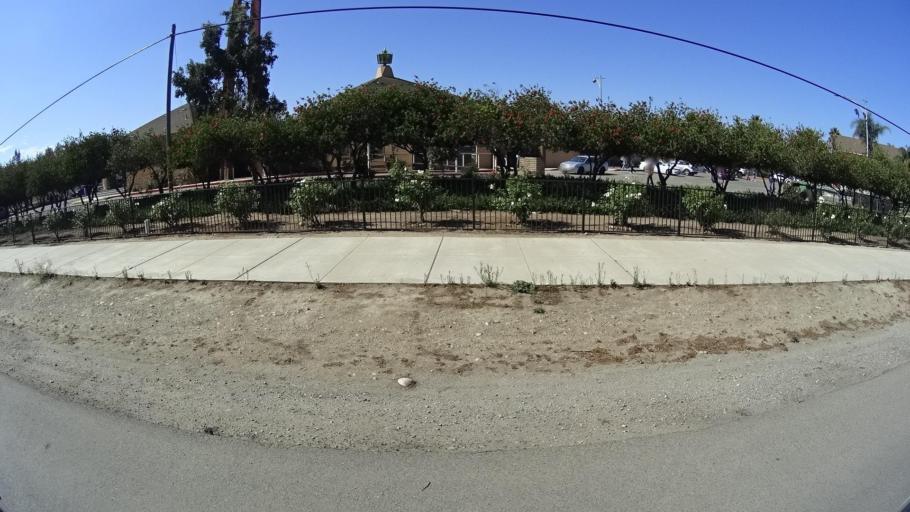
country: US
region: California
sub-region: Monterey County
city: Greenfield
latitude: 36.3173
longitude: -121.2403
